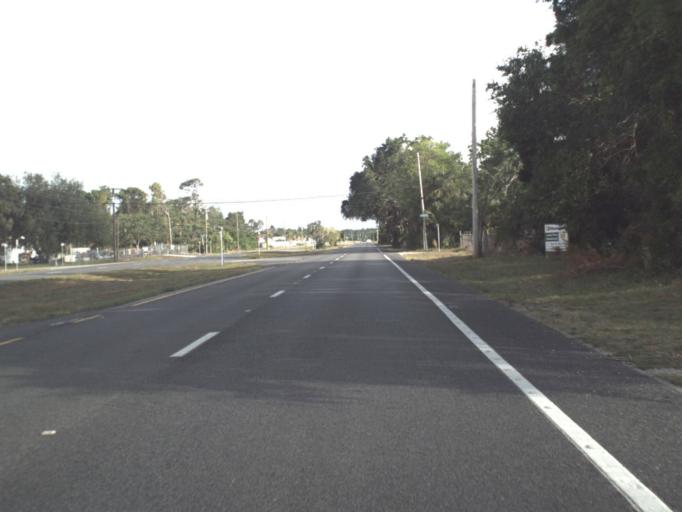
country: US
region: Florida
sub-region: Brevard County
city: Mims
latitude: 28.7605
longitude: -80.8759
